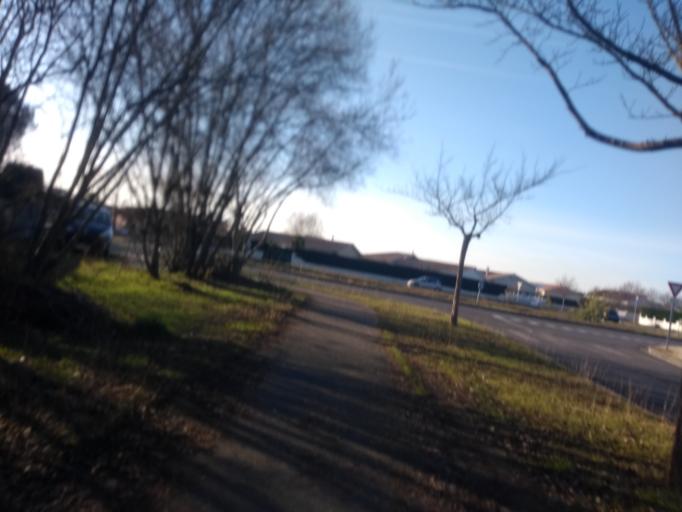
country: FR
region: Aquitaine
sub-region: Departement de la Gironde
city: Le Barp
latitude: 44.6065
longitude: -0.7766
